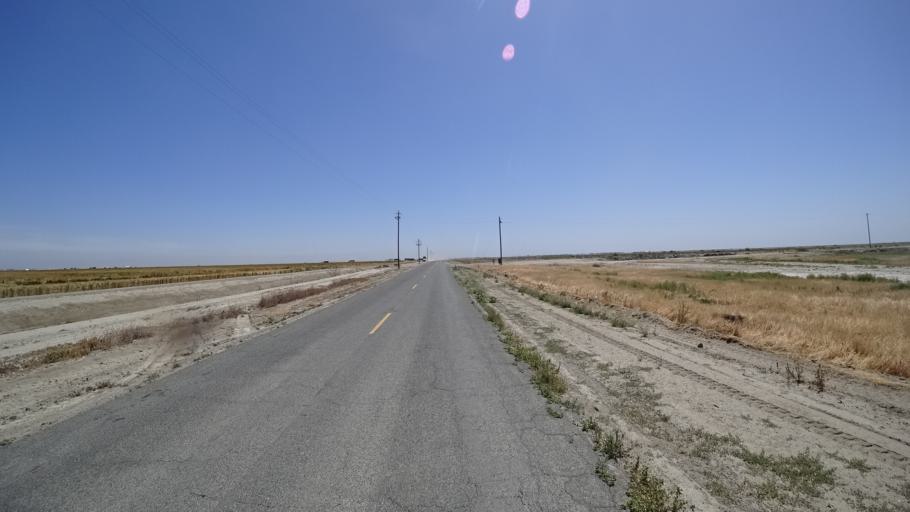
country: US
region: California
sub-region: Kings County
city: Stratford
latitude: 36.1379
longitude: -119.6993
